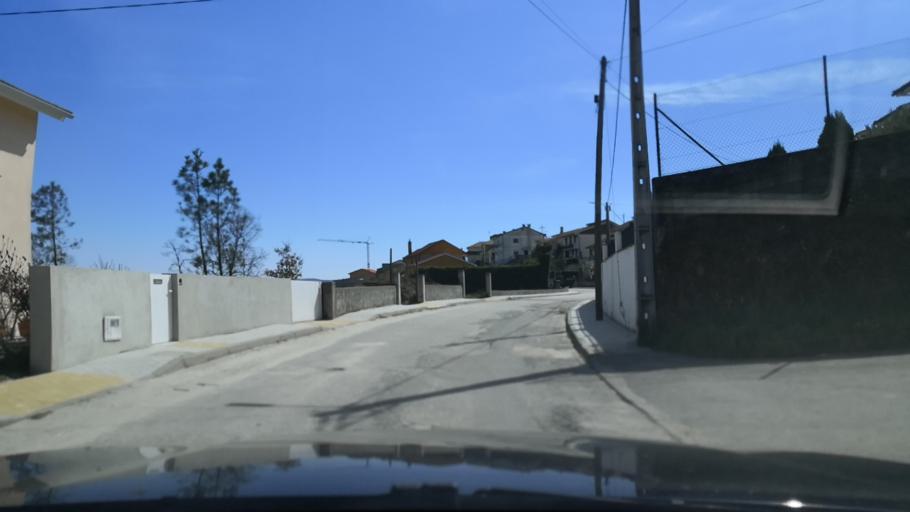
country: PT
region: Vila Real
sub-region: Sabrosa
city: Sabrosa
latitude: 41.3398
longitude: -7.5925
